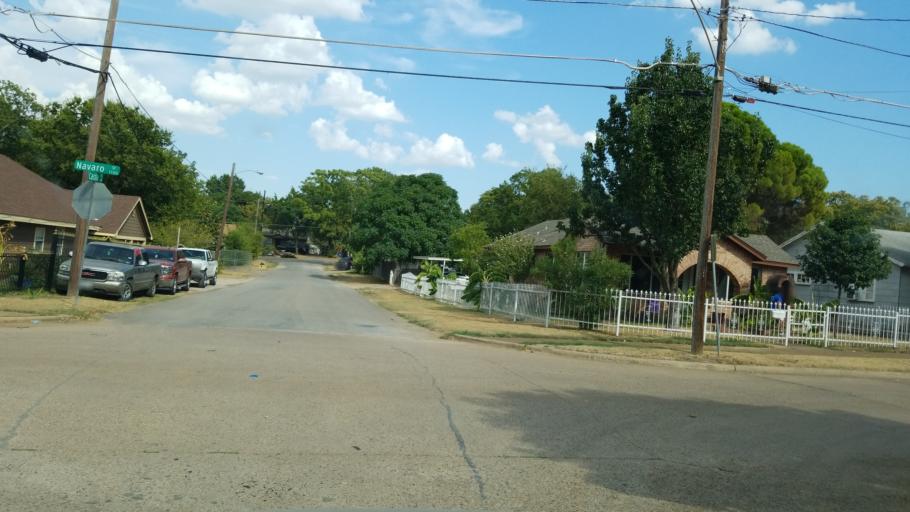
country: US
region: Texas
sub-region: Dallas County
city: Dallas
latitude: 32.7673
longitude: -96.8471
